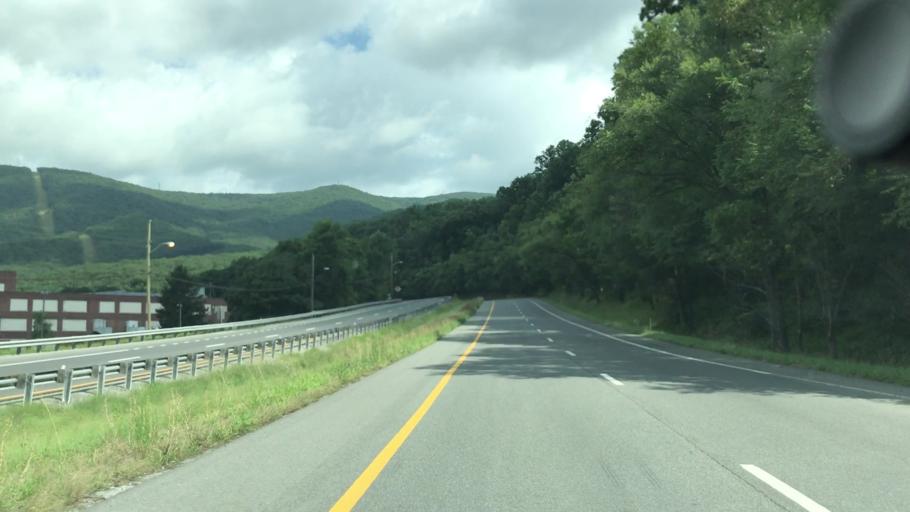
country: US
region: Virginia
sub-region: Giles County
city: Pearisburg
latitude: 37.3437
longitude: -80.7593
